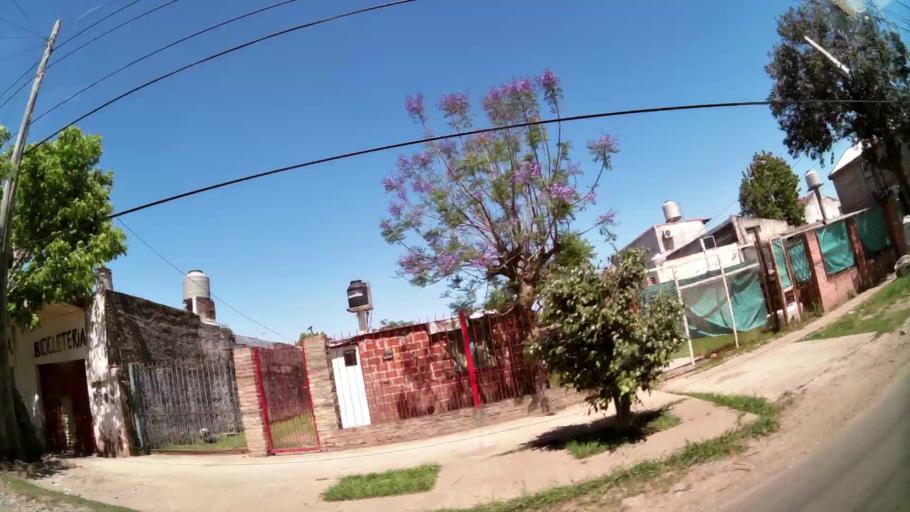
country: AR
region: Buenos Aires
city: Hurlingham
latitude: -34.4967
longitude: -58.6597
